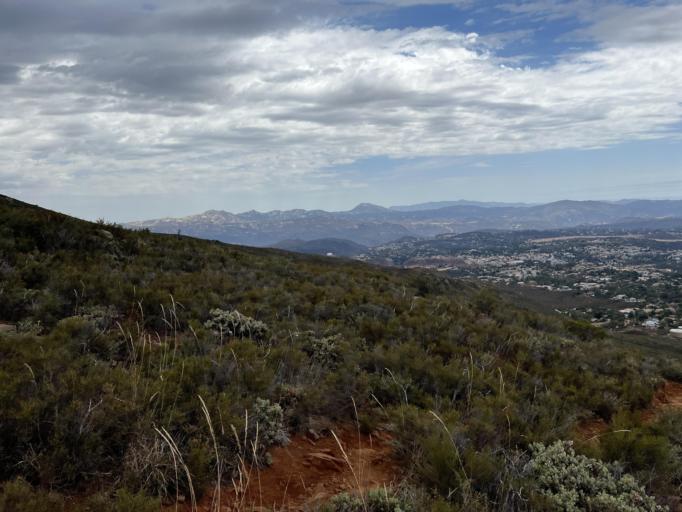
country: US
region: California
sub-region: San Diego County
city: Alpine
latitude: 32.8587
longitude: -116.7363
